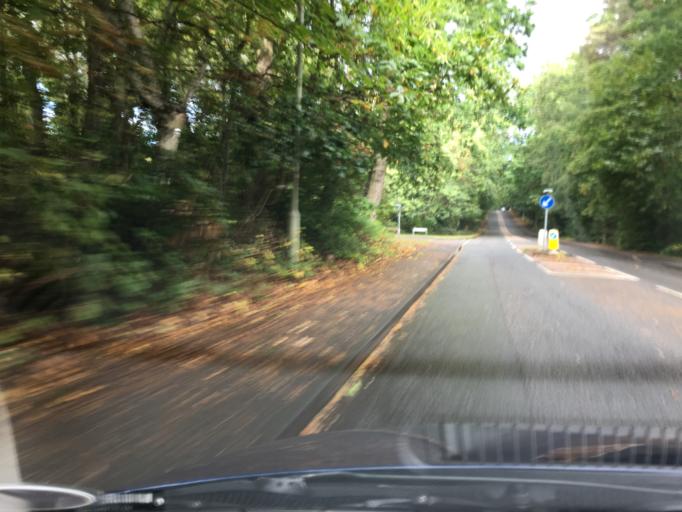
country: GB
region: England
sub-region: Bracknell Forest
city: Crowthorne
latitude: 51.3784
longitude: -0.8051
